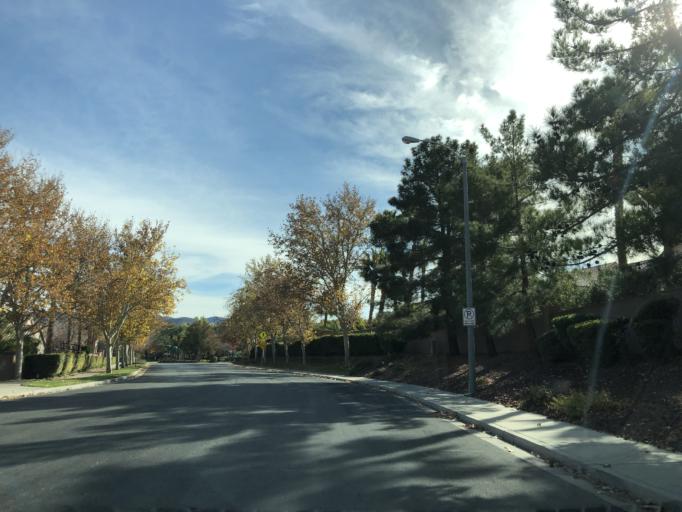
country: US
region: Nevada
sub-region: Clark County
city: Whitney
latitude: 36.0162
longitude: -115.0809
